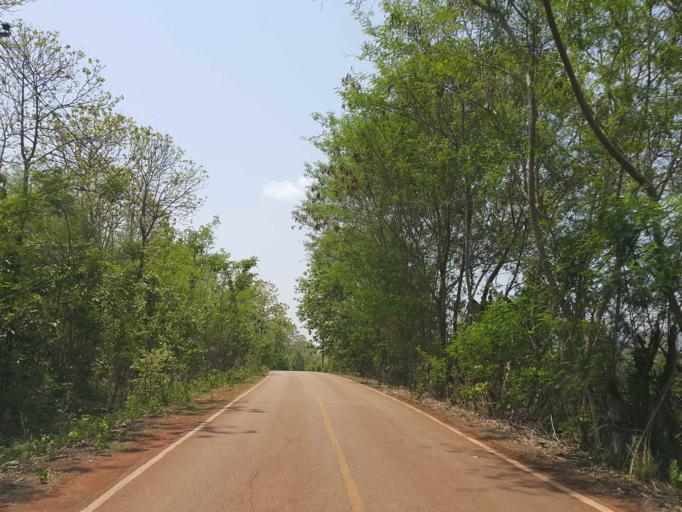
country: TH
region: Chiang Mai
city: Mae Taeng
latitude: 19.0873
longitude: 99.0871
